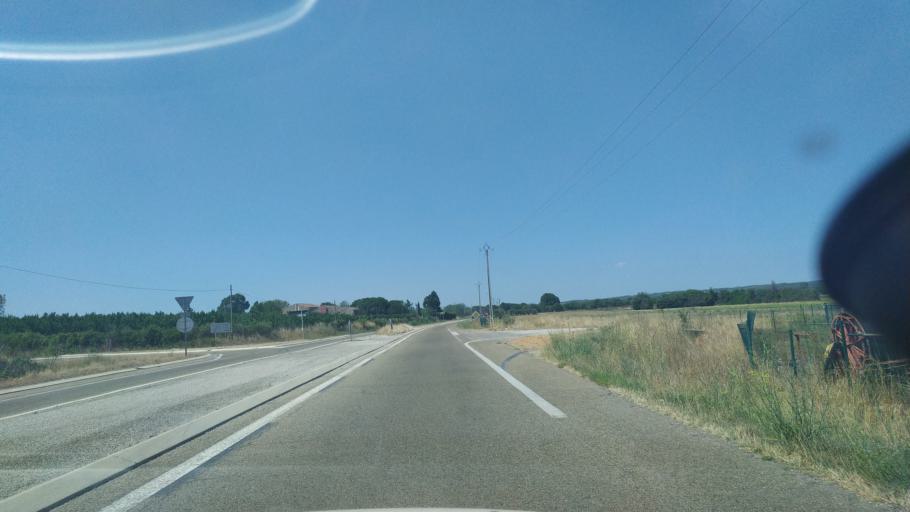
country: FR
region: Languedoc-Roussillon
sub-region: Departement du Gard
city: Caissargues
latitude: 43.7793
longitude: 4.3471
